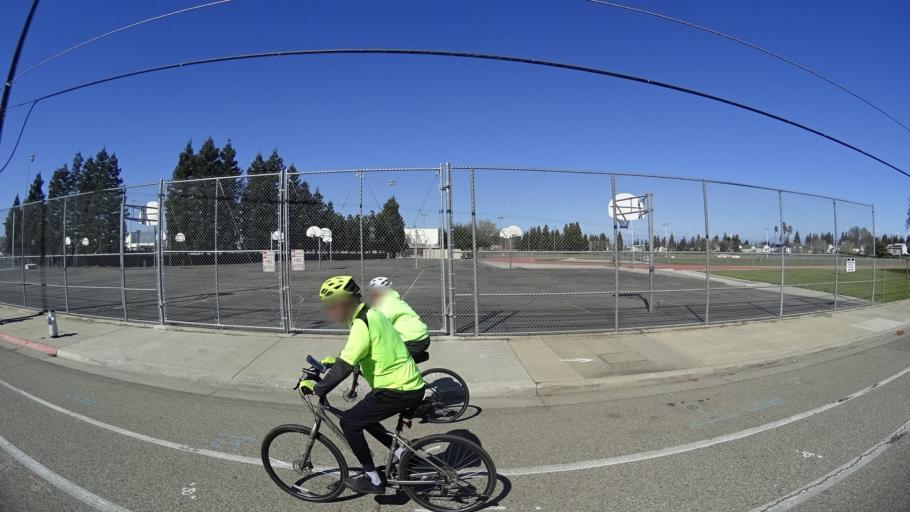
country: US
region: California
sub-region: Fresno County
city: Clovis
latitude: 36.8592
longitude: -119.7614
